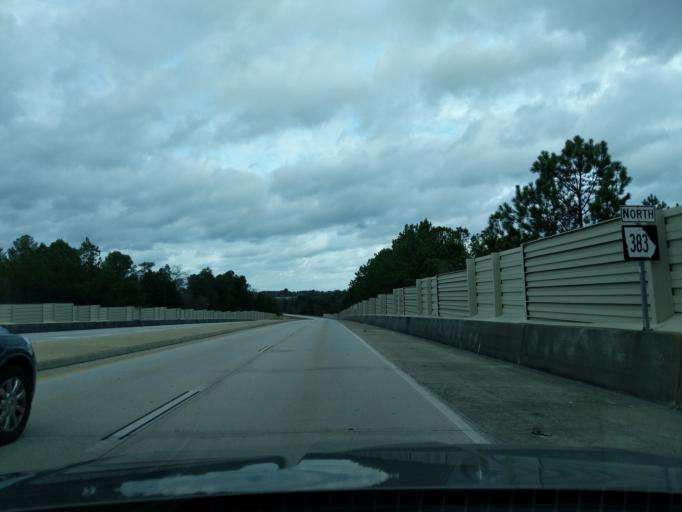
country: US
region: Georgia
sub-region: Columbia County
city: Martinez
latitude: 33.4610
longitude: -82.1190
